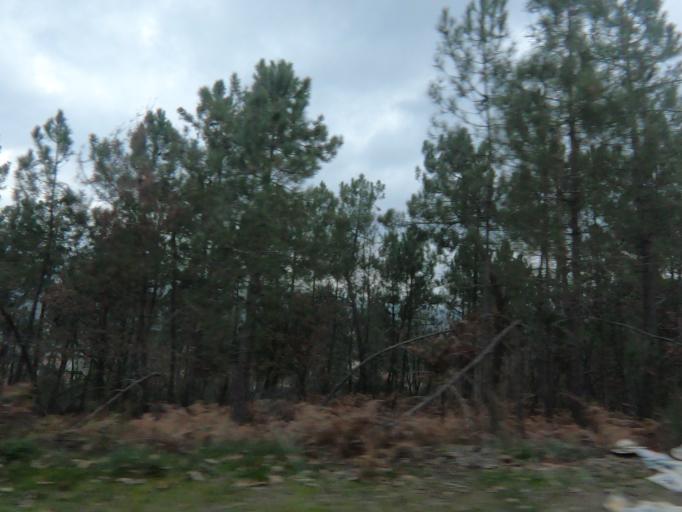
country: PT
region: Vila Real
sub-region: Vila Real
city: Vila Real
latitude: 41.3380
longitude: -7.6586
